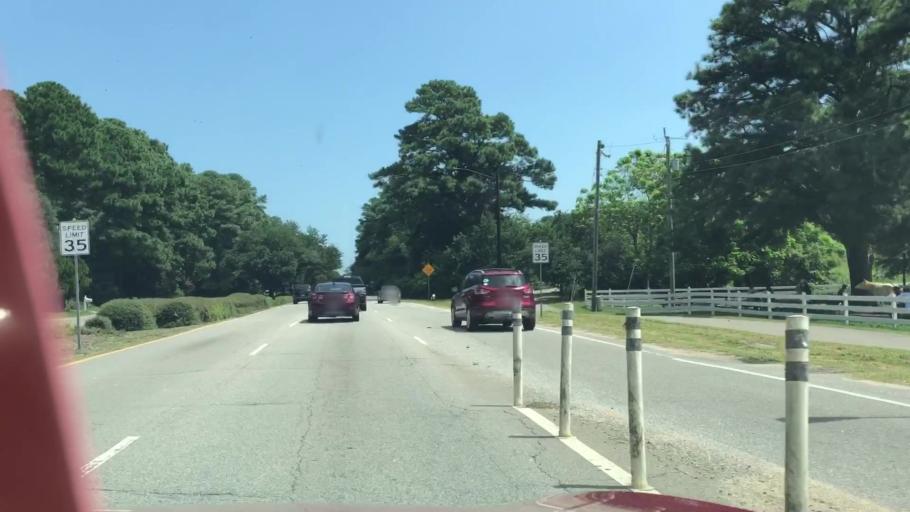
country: US
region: Virginia
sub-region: City of Virginia Beach
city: Virginia Beach
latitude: 36.9062
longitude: -76.1163
